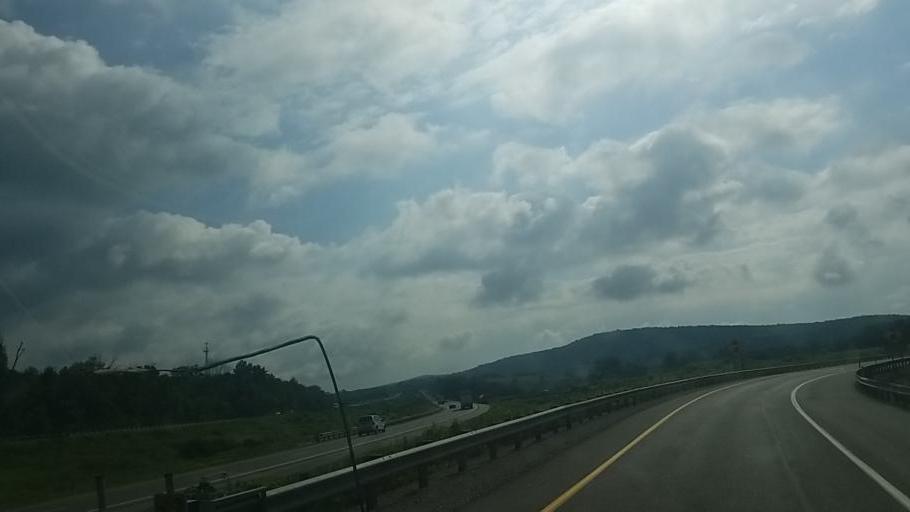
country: US
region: Pennsylvania
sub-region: Centre County
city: Zion
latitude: 40.9437
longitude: -77.7279
